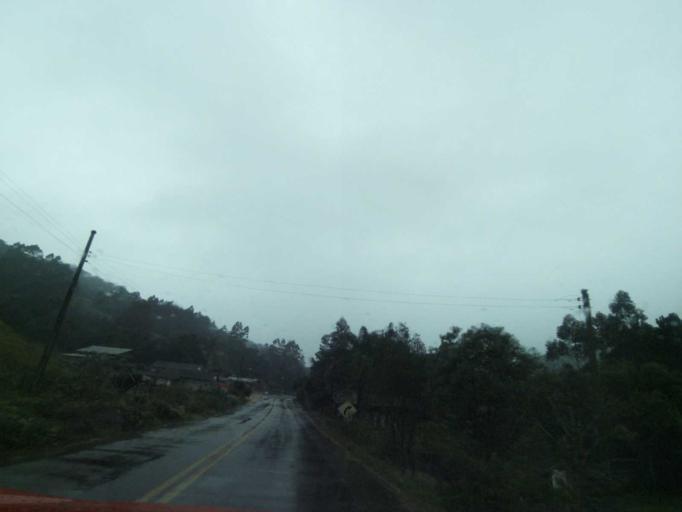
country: BR
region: Santa Catarina
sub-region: Anitapolis
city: Anitapolis
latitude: -27.8211
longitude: -49.0491
